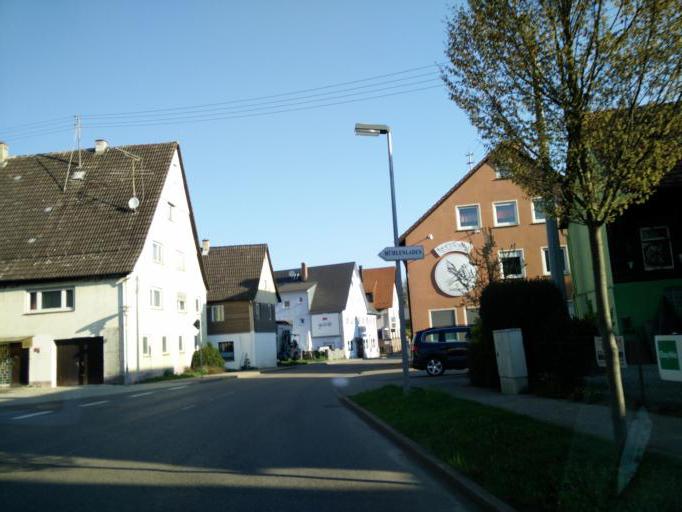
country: DE
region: Baden-Wuerttemberg
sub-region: Regierungsbezirk Stuttgart
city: Deckenpfronn
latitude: 48.6232
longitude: 8.8350
